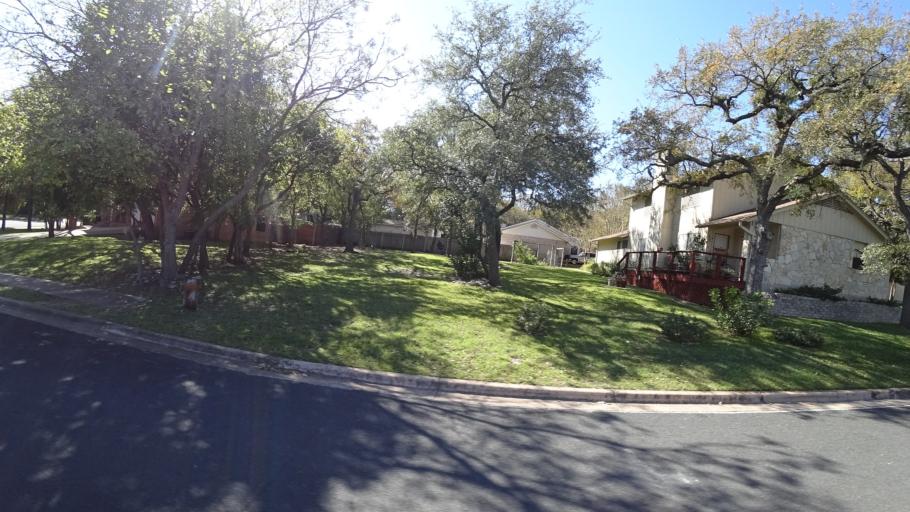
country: US
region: Texas
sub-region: Williamson County
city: Jollyville
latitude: 30.4189
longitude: -97.7609
